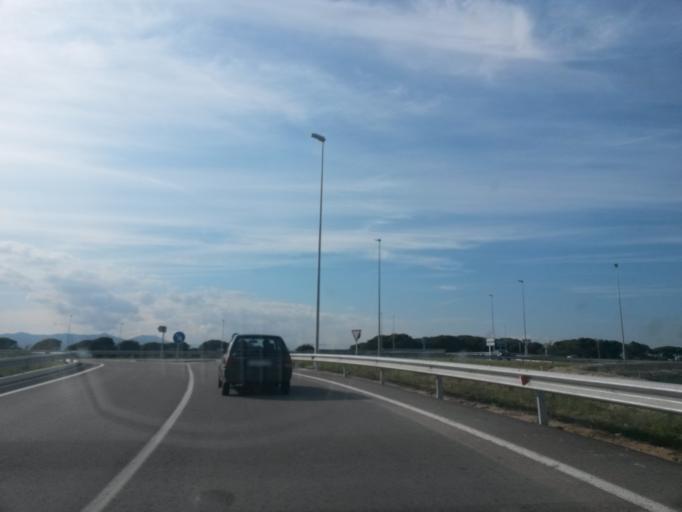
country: ES
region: Catalonia
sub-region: Provincia de Girona
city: Vilobi d'Onyar
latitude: 41.8507
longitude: 2.7732
